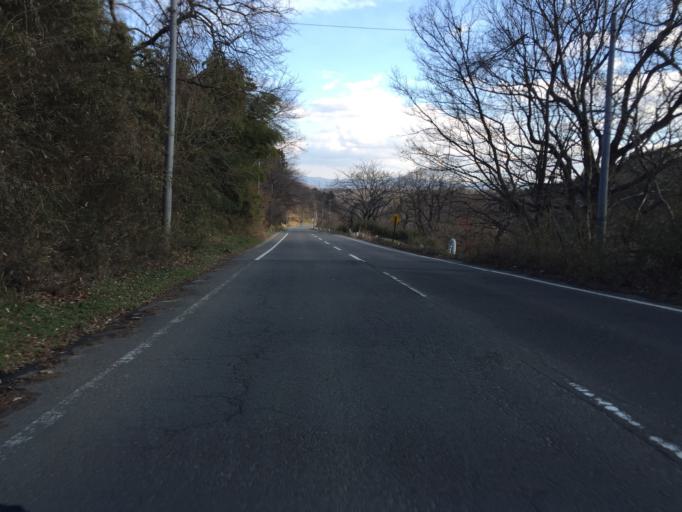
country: JP
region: Fukushima
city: Fukushima-shi
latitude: 37.6860
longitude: 140.4182
